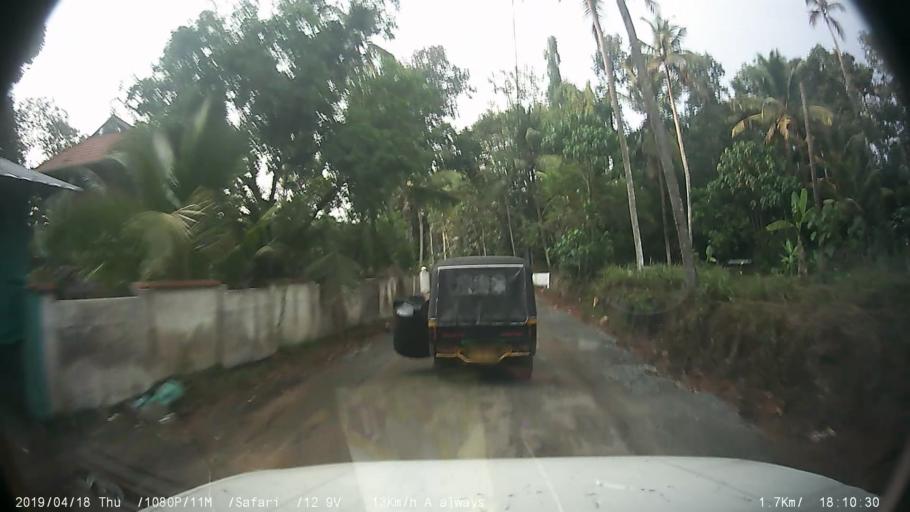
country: IN
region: Kerala
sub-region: Kottayam
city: Palackattumala
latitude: 9.7785
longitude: 76.5779
